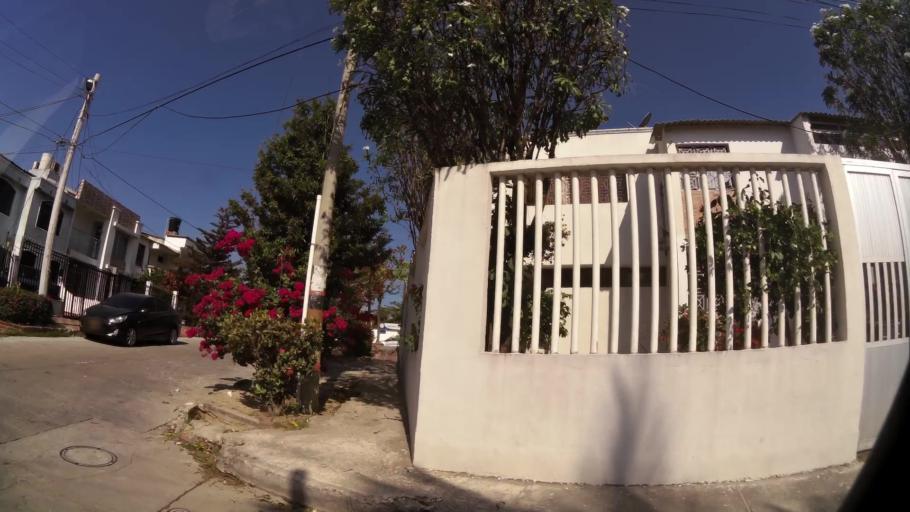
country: CO
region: Atlantico
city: Barranquilla
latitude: 10.9872
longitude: -74.8308
